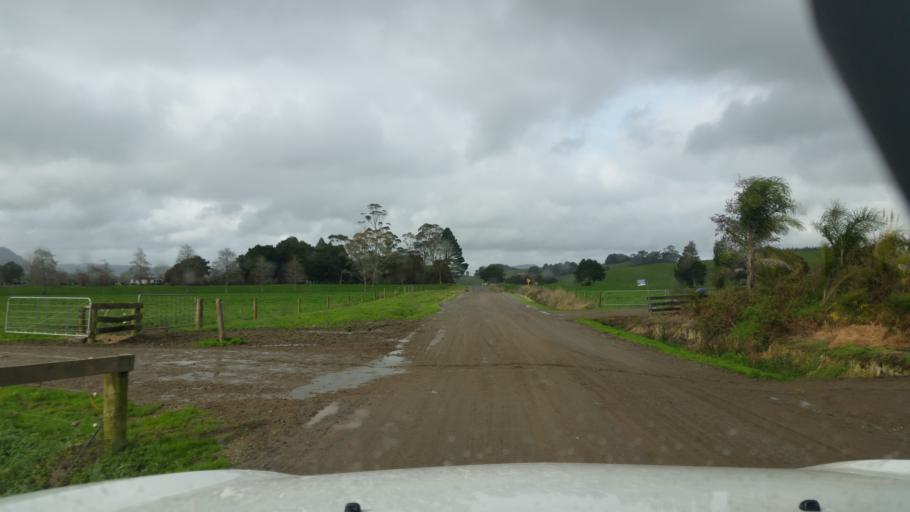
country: NZ
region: Northland
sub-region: Whangarei
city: Maungatapere
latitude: -35.6105
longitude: 174.1819
